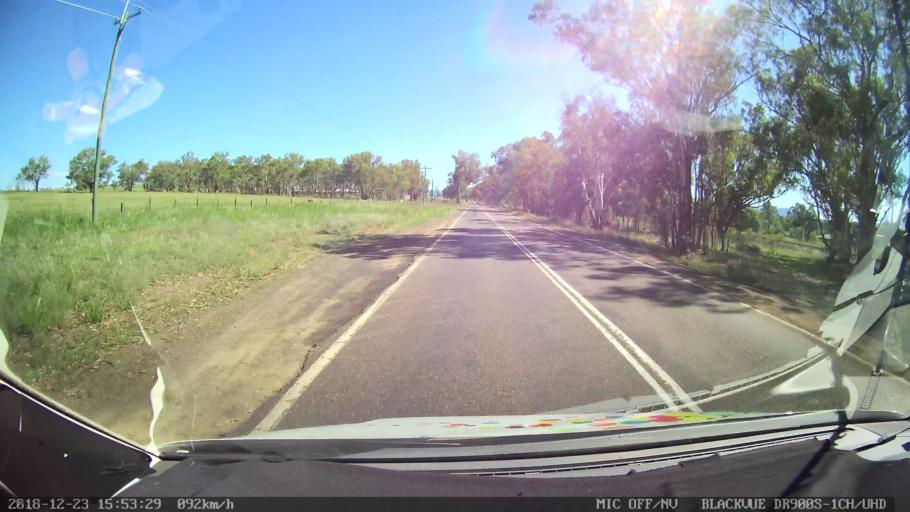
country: AU
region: New South Wales
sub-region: Tamworth Municipality
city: Phillip
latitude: -31.1336
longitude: 150.8806
